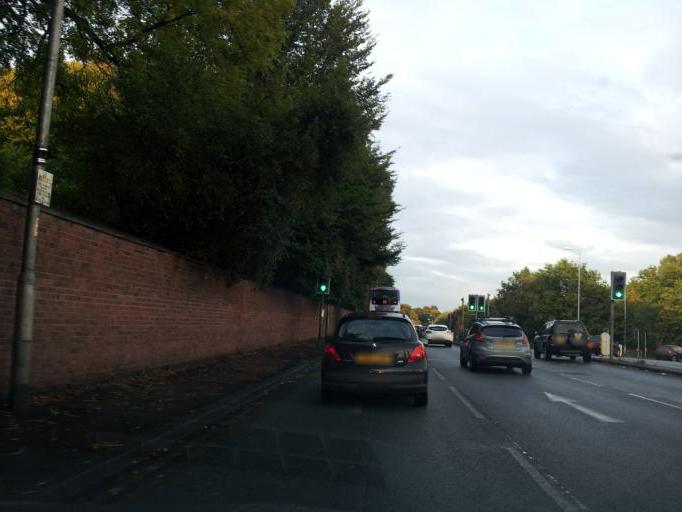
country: GB
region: England
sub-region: Manchester
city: Crumpsall
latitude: 53.5327
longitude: -2.2449
